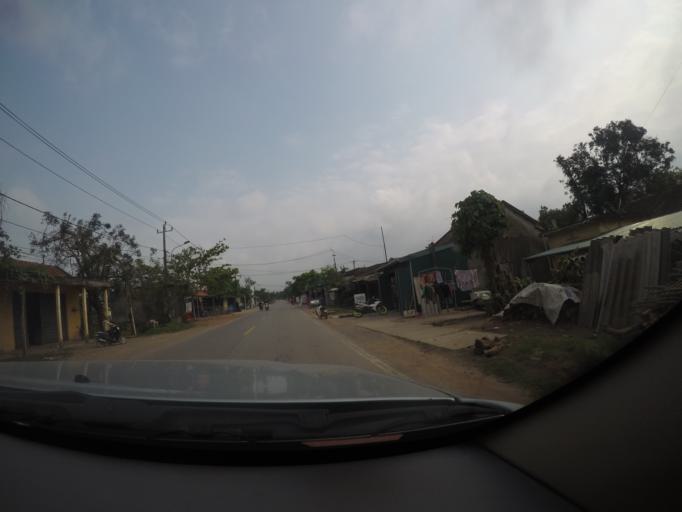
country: VN
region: Quang Binh
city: Kwang Binh
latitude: 17.4650
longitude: 106.5590
